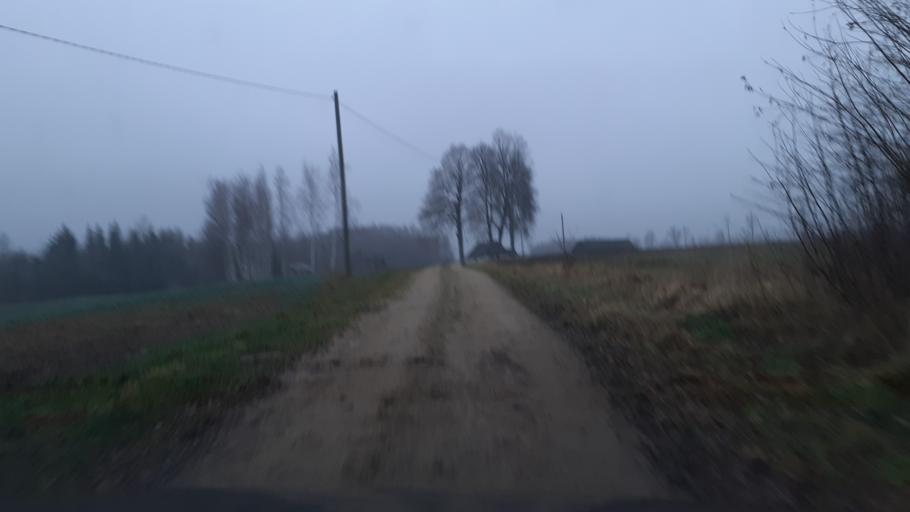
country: LV
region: Alsunga
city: Alsunga
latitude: 56.8922
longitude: 21.6702
